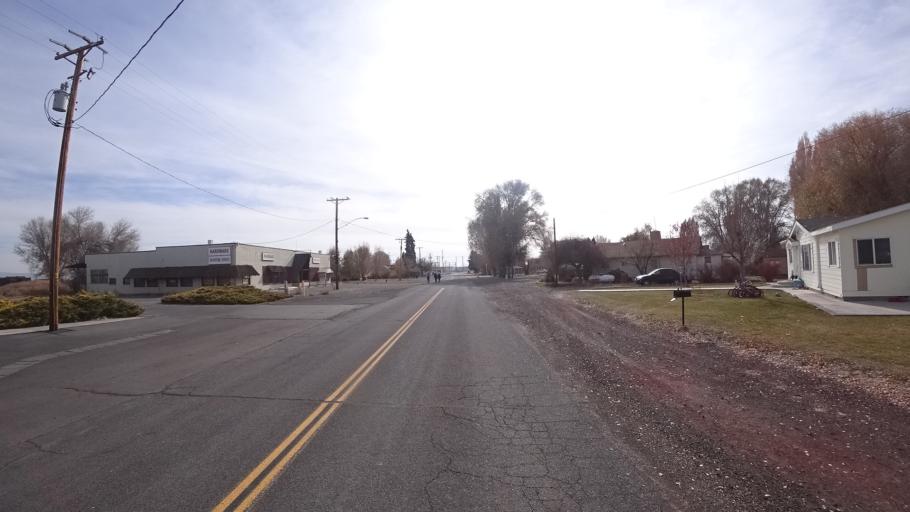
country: US
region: California
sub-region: Siskiyou County
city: Tulelake
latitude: 41.9557
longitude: -121.4743
